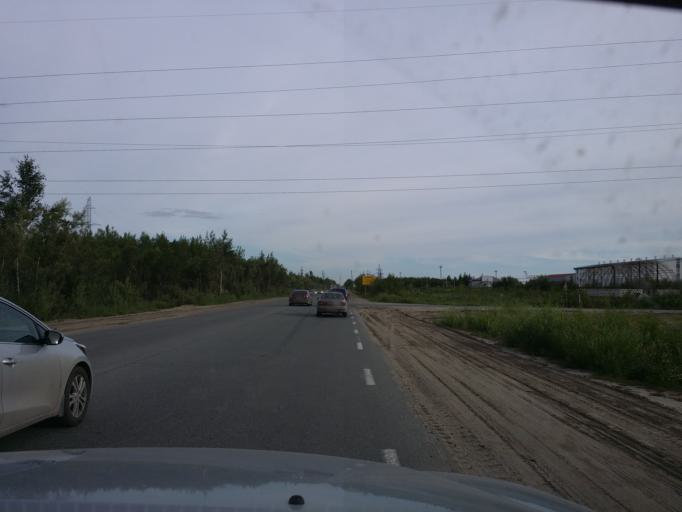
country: RU
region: Khanty-Mansiyskiy Avtonomnyy Okrug
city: Nizhnevartovsk
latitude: 60.9600
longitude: 76.6627
